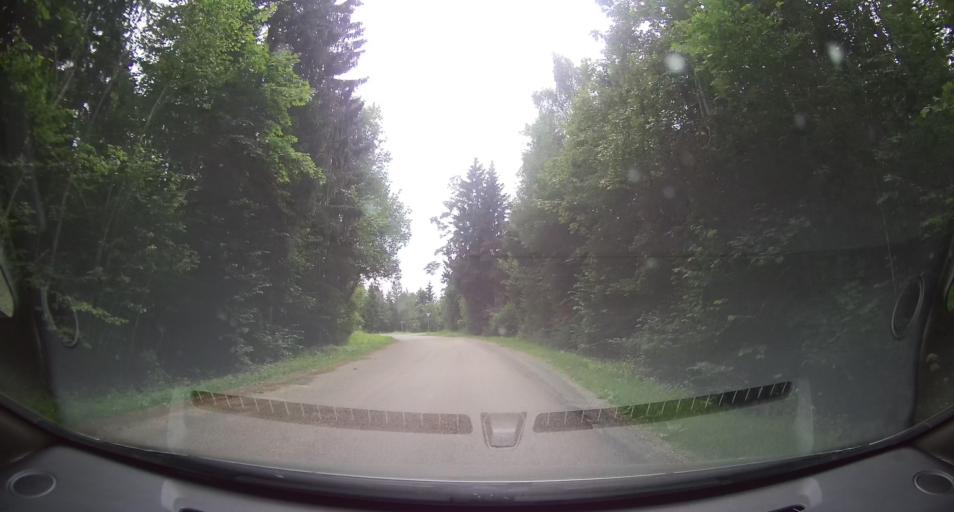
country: EE
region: Harju
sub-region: Keila linn
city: Keila
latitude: 59.2402
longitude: 24.4857
